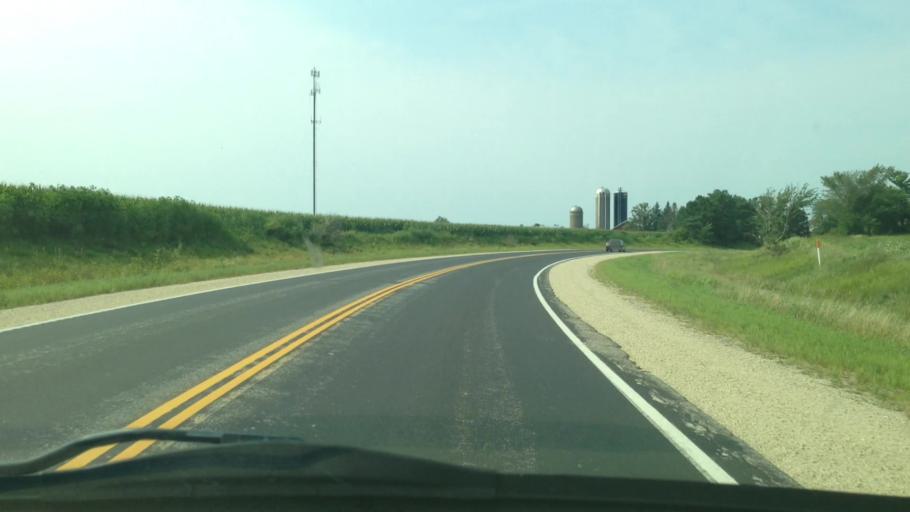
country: US
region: Minnesota
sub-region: Winona County
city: Lewiston
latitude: 43.9291
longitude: -91.9595
